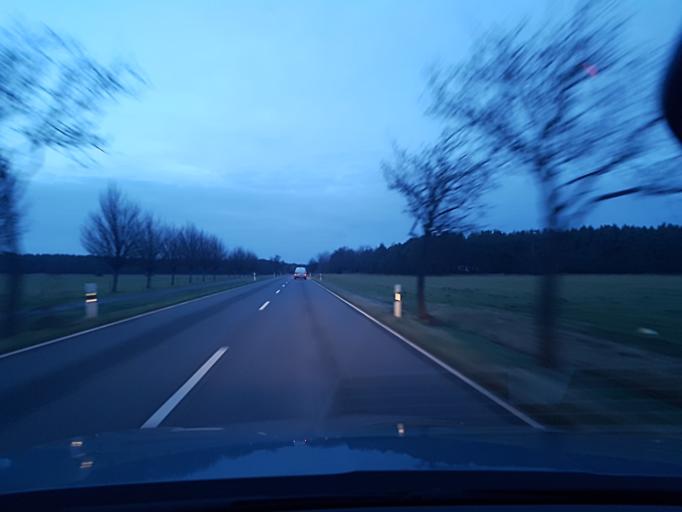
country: DE
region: Brandenburg
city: Ruckersdorf
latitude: 51.5777
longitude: 13.5638
